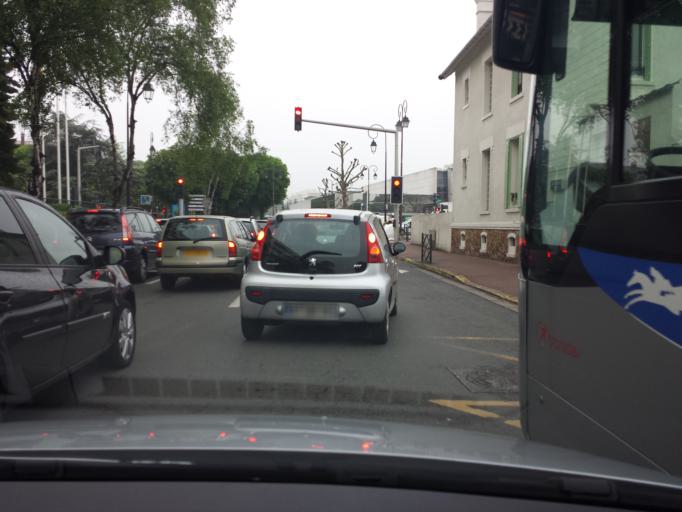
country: FR
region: Ile-de-France
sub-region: Departement des Hauts-de-Seine
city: Antony
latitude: 48.7539
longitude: 2.3001
